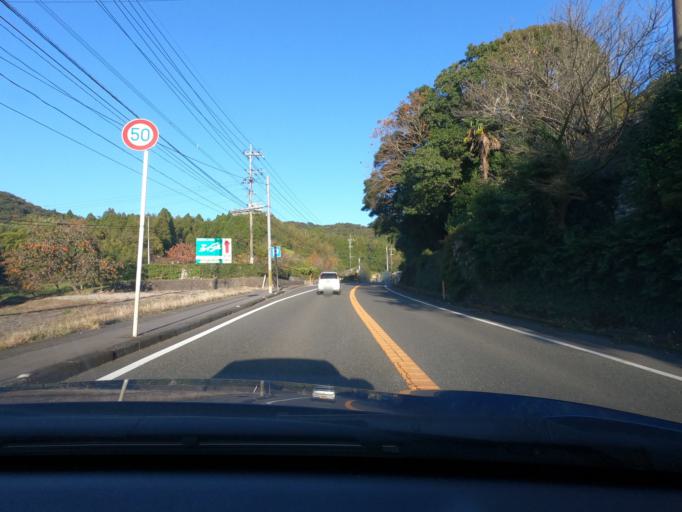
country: JP
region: Kagoshima
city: Satsumasendai
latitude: 31.8507
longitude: 130.2638
